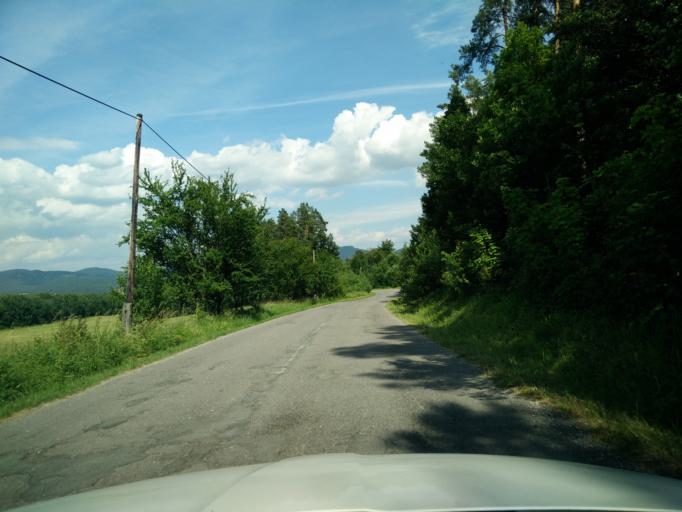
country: SK
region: Nitriansky
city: Bojnice
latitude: 48.8755
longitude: 18.6039
